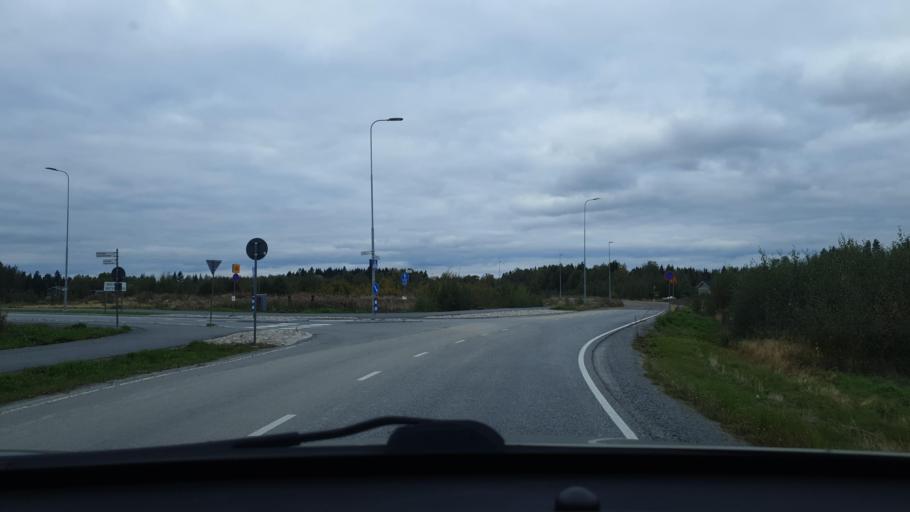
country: FI
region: Ostrobothnia
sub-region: Vaasa
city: Korsholm
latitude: 63.1289
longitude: 21.6603
